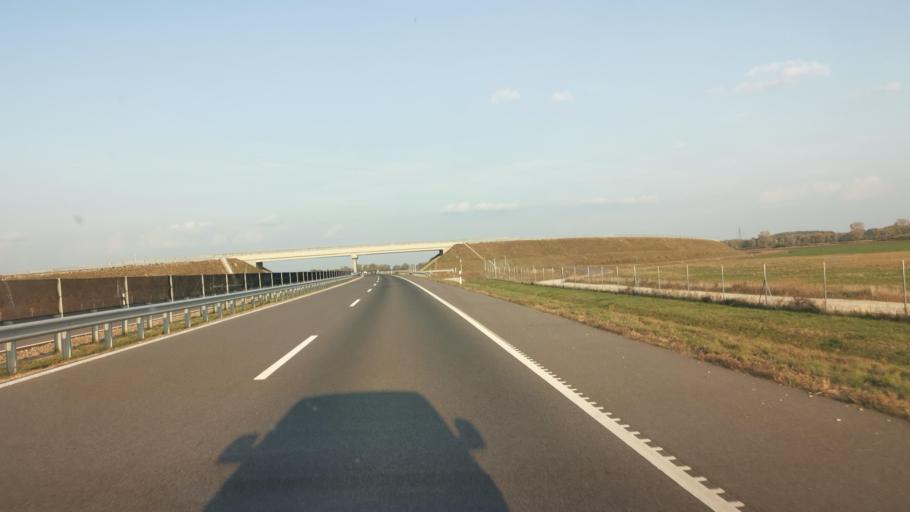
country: HU
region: Gyor-Moson-Sopron
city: Mihalyi
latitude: 47.5675
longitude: 17.1379
